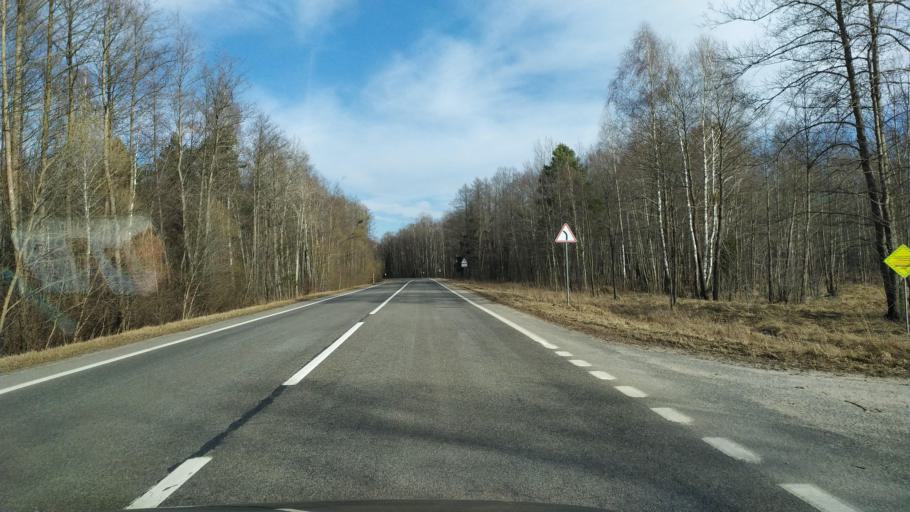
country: BY
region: Brest
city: Pruzhany
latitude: 52.4817
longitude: 24.1636
